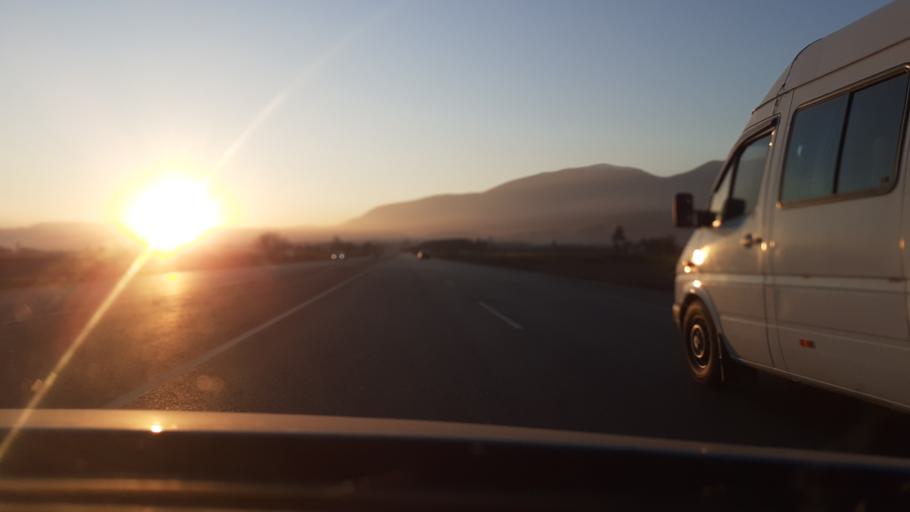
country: TR
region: Hatay
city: Kirikhan
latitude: 36.5042
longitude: 36.4064
